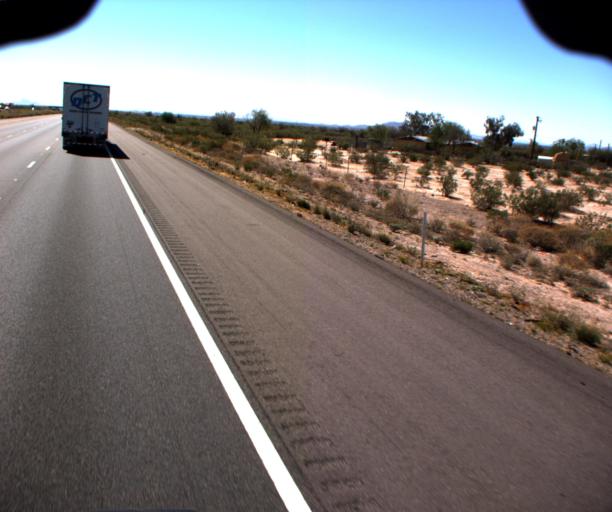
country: US
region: Arizona
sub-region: Pinal County
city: Casa Grande
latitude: 32.9758
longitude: -111.7314
